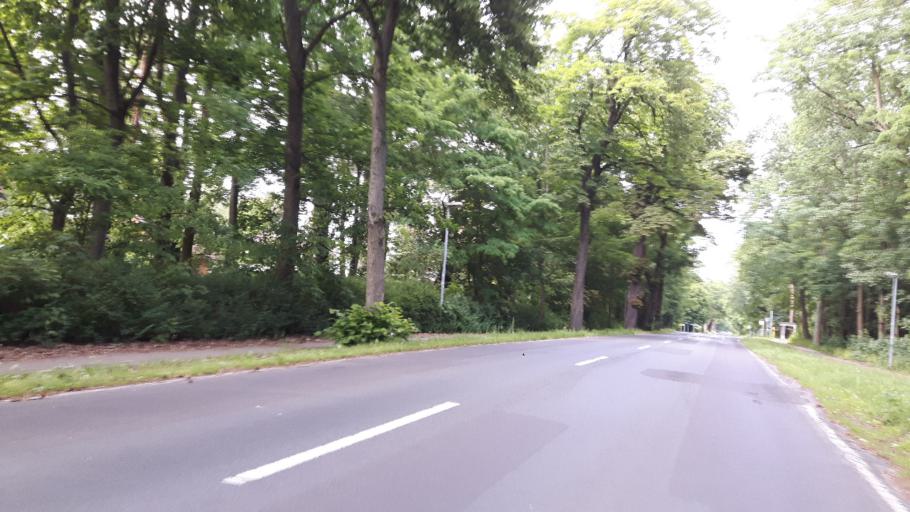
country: DE
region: Brandenburg
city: Michendorf
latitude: 52.3197
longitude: 13.0338
